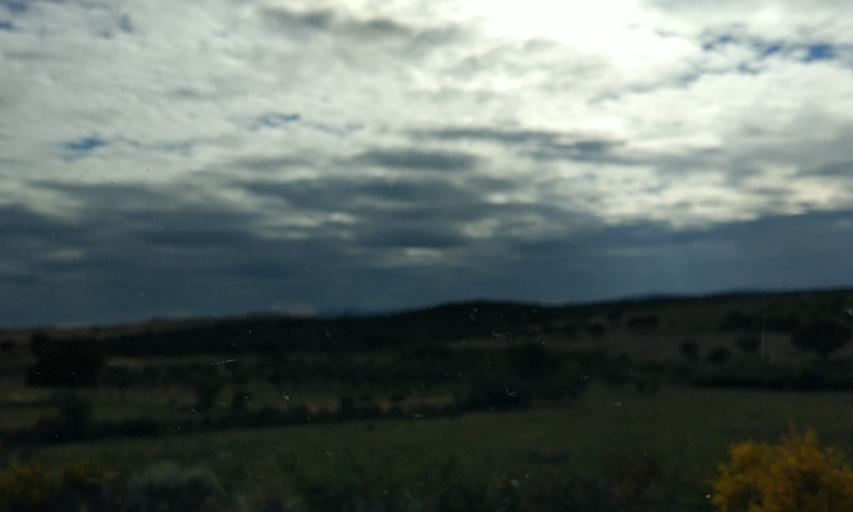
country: ES
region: Extremadura
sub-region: Provincia de Caceres
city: Perales del Puerto
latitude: 40.1121
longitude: -6.6708
